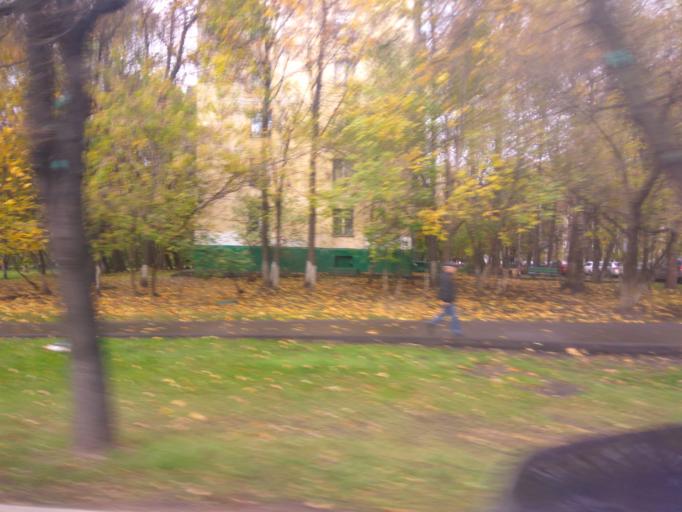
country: RU
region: Moscow
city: Tsaritsyno
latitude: 55.6280
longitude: 37.6539
